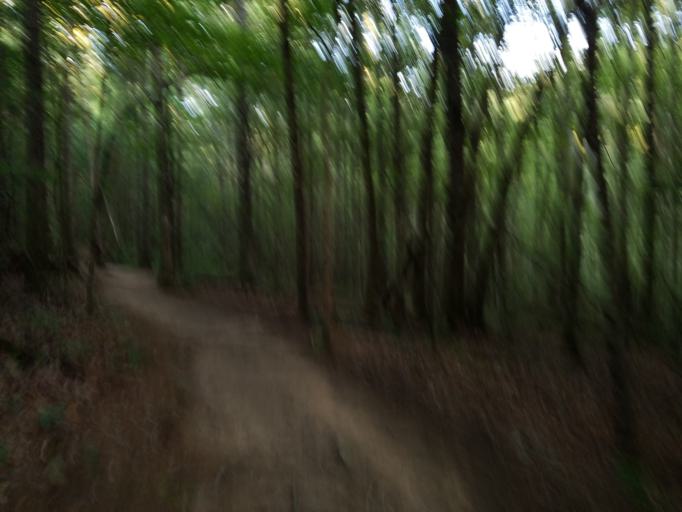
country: US
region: Georgia
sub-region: Fannin County
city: Blue Ridge
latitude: 34.7377
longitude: -84.1699
